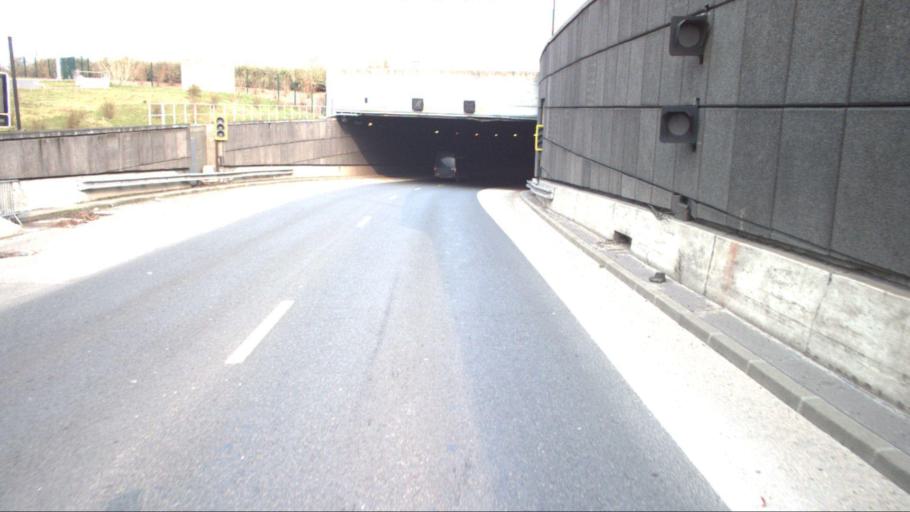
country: FR
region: Ile-de-France
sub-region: Departement des Yvelines
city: Chatou
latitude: 48.8717
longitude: 2.1580
